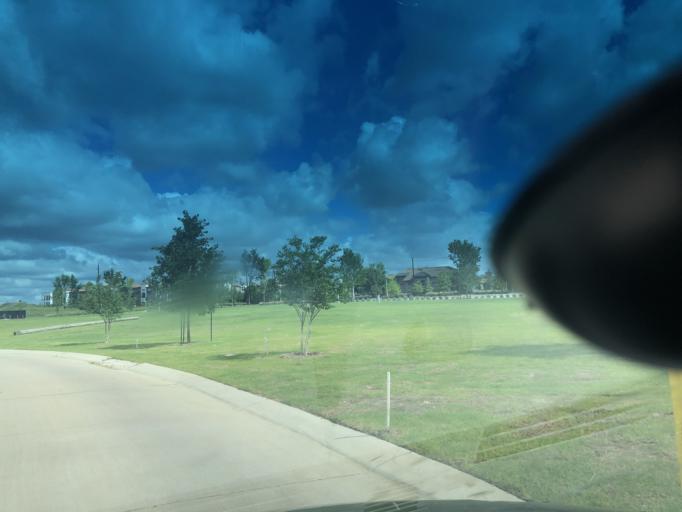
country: US
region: Texas
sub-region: Dallas County
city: Grand Prairie
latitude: 32.7015
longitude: -97.0331
